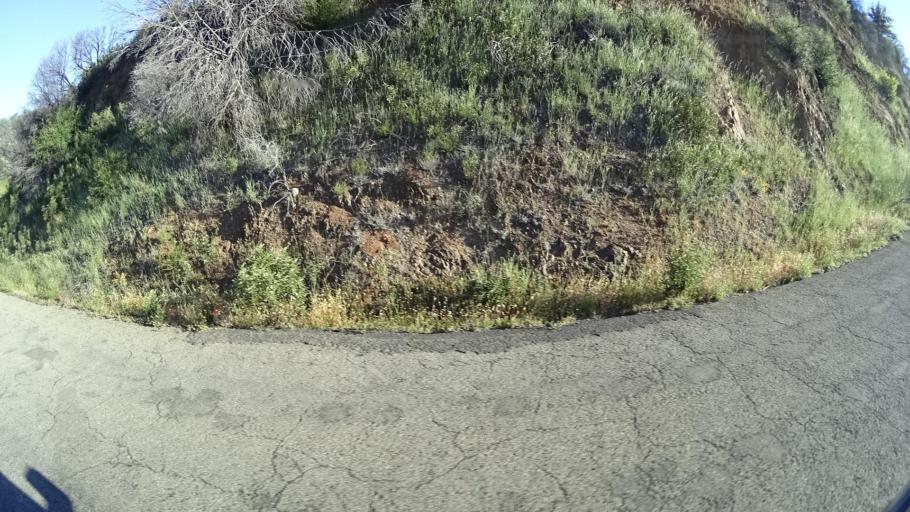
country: US
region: California
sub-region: Lake County
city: Upper Lake
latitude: 39.2579
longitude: -122.9446
